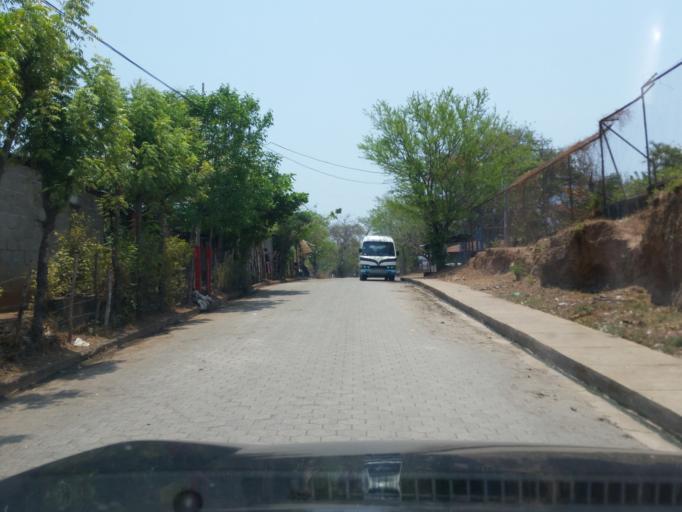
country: NI
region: Granada
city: Granada
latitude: 11.9108
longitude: -85.9535
